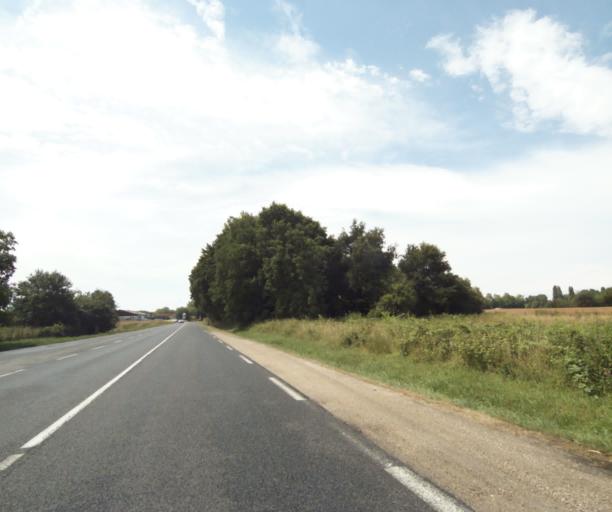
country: FR
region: Ile-de-France
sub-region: Departement de Seine-et-Marne
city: Cely
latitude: 48.4659
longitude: 2.5379
